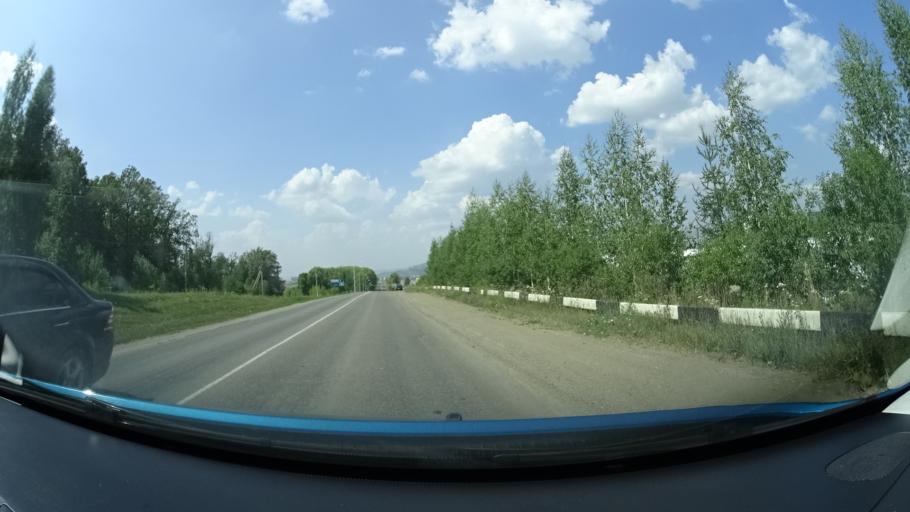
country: RU
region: Bashkortostan
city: Oktyabr'skiy
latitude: 54.4794
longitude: 53.5606
